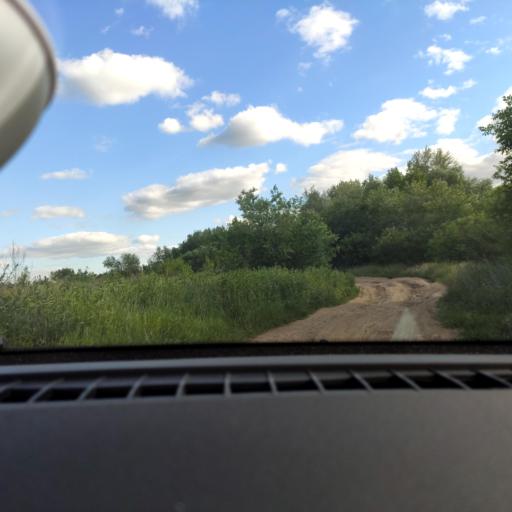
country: RU
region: Samara
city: Samara
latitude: 53.1790
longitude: 50.2371
